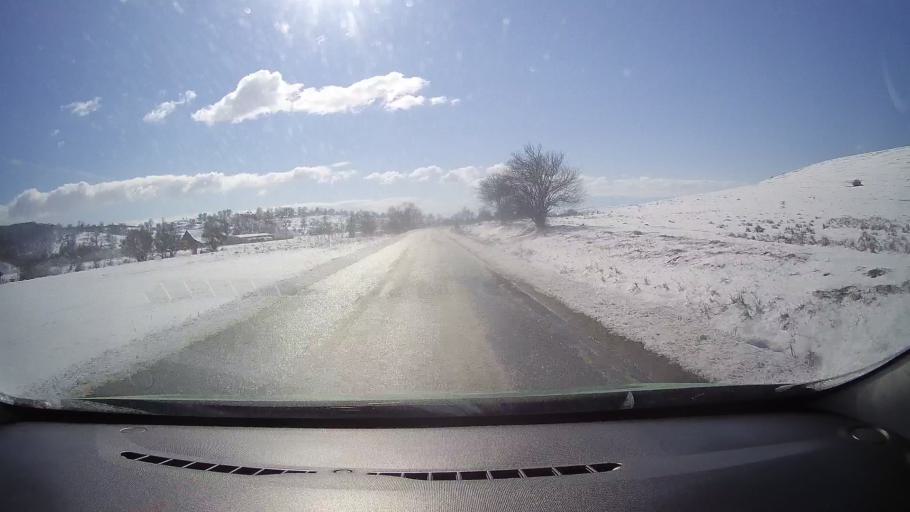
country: RO
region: Sibiu
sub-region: Comuna Rosia
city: Rosia
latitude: 45.8628
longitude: 24.3184
